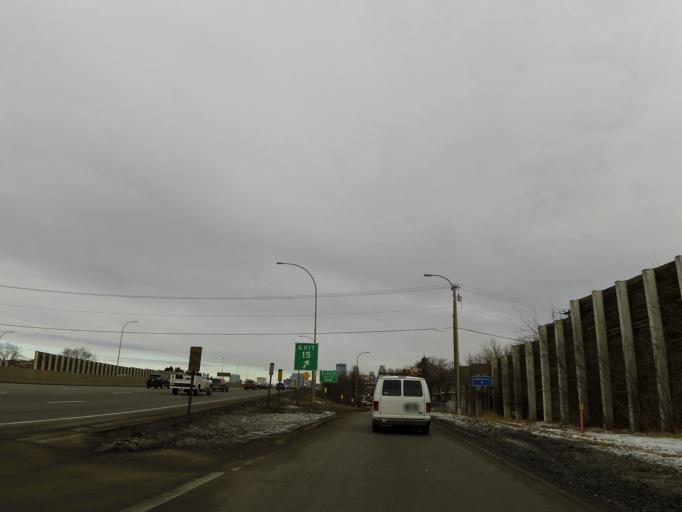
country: US
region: Minnesota
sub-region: Hennepin County
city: Minneapolis
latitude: 44.9445
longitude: -93.2744
